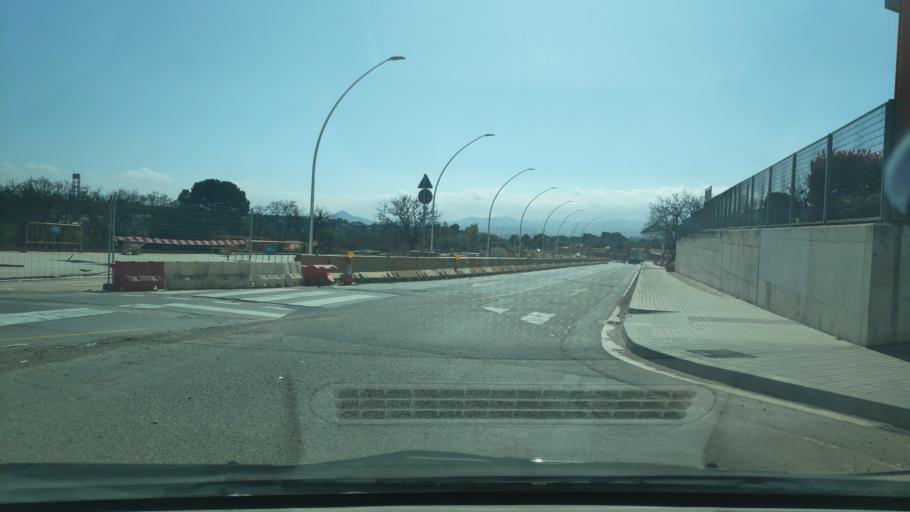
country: ES
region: Catalonia
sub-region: Provincia de Barcelona
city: Barbera del Valles
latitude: 41.5345
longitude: 2.1330
